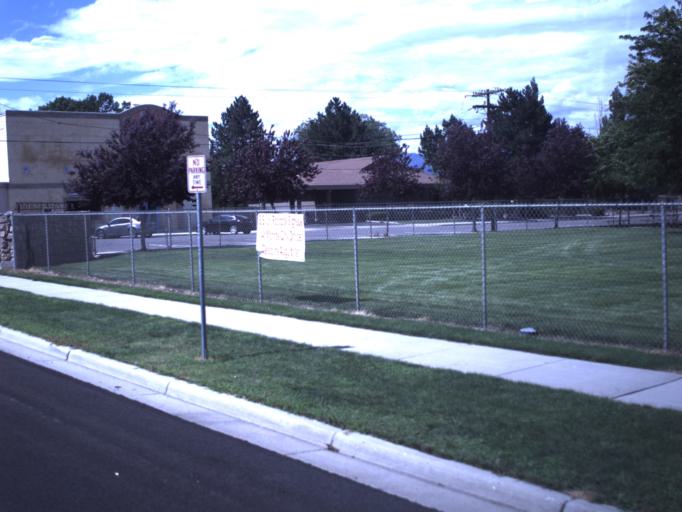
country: US
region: Utah
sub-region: Sevier County
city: Monroe
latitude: 38.6324
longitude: -112.1215
